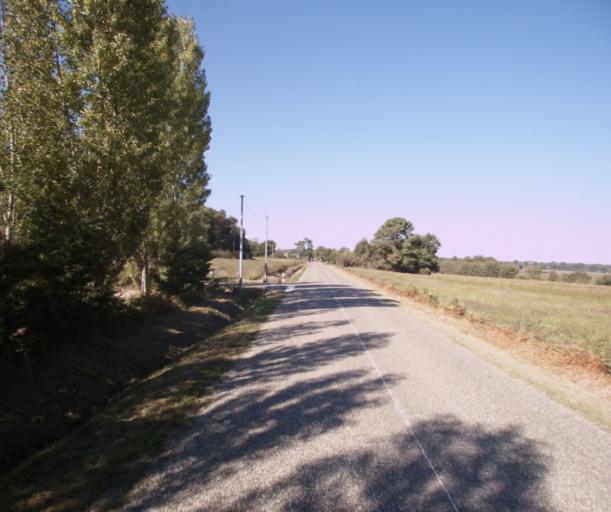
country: FR
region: Aquitaine
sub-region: Departement des Landes
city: Gabarret
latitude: 43.9507
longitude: 0.0017
